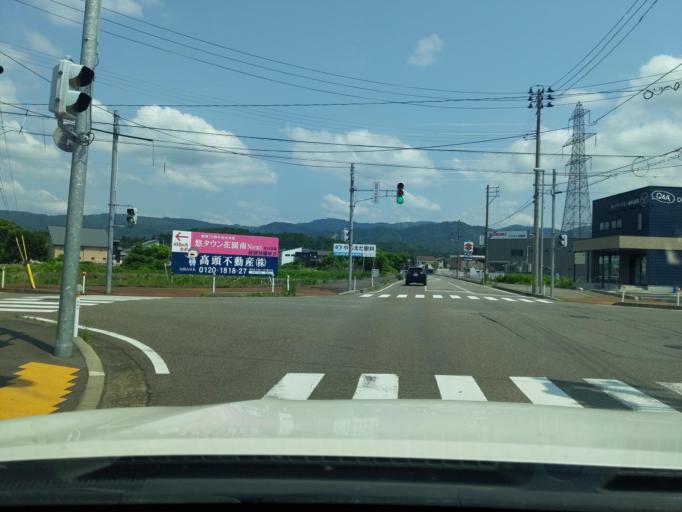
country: JP
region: Niigata
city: Nagaoka
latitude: 37.4280
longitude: 138.8587
